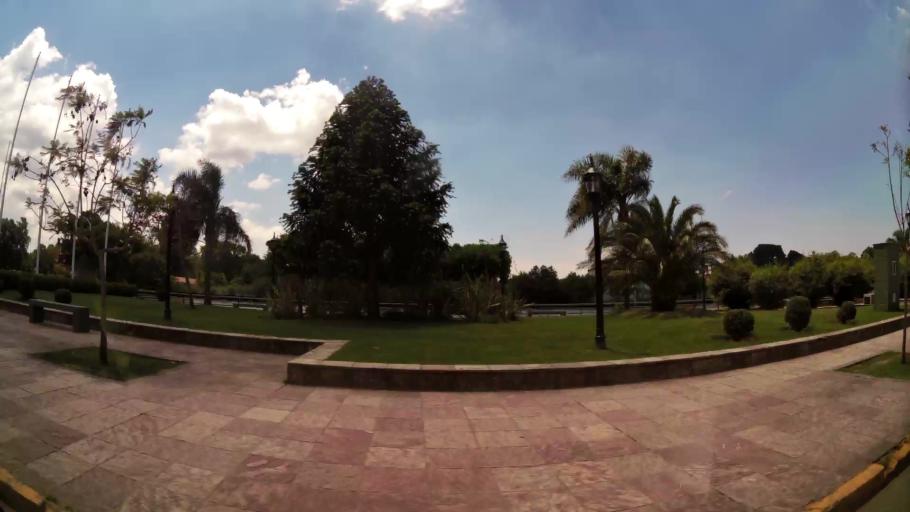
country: AR
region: Buenos Aires
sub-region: Partido de Tigre
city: Tigre
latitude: -34.4106
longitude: -58.5887
